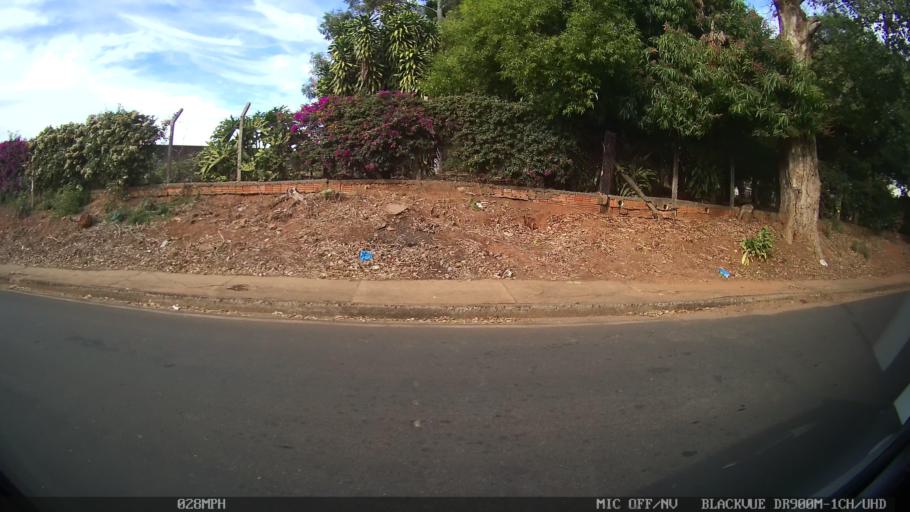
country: BR
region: Sao Paulo
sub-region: Catanduva
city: Catanduva
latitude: -21.1378
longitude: -48.9953
